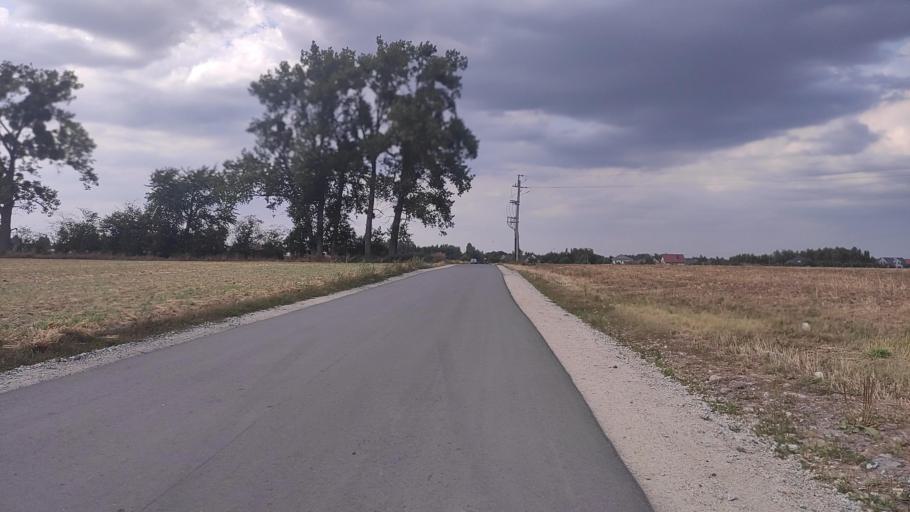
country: PL
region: Greater Poland Voivodeship
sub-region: Powiat poznanski
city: Swarzedz
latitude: 52.4162
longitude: 17.1018
